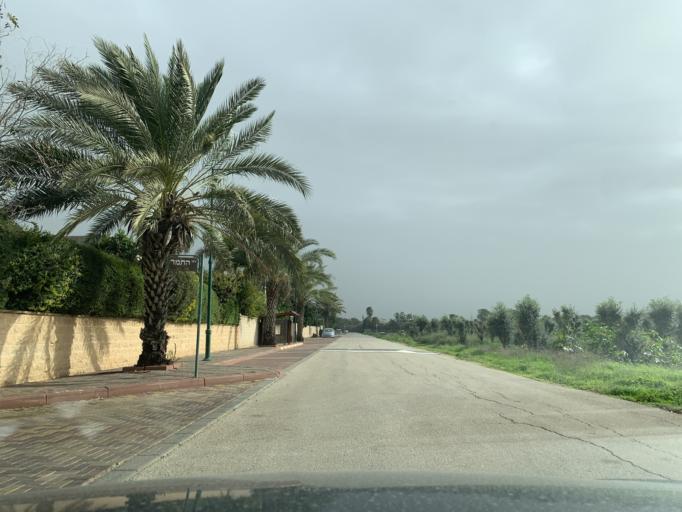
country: IL
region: Central District
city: Jaljulya
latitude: 32.1572
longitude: 34.9390
